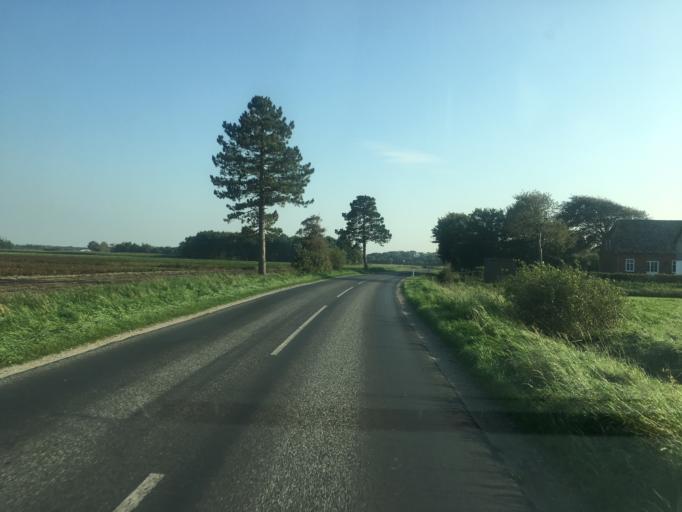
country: DE
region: Schleswig-Holstein
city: Bramstedtlund
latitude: 54.9406
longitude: 9.0658
